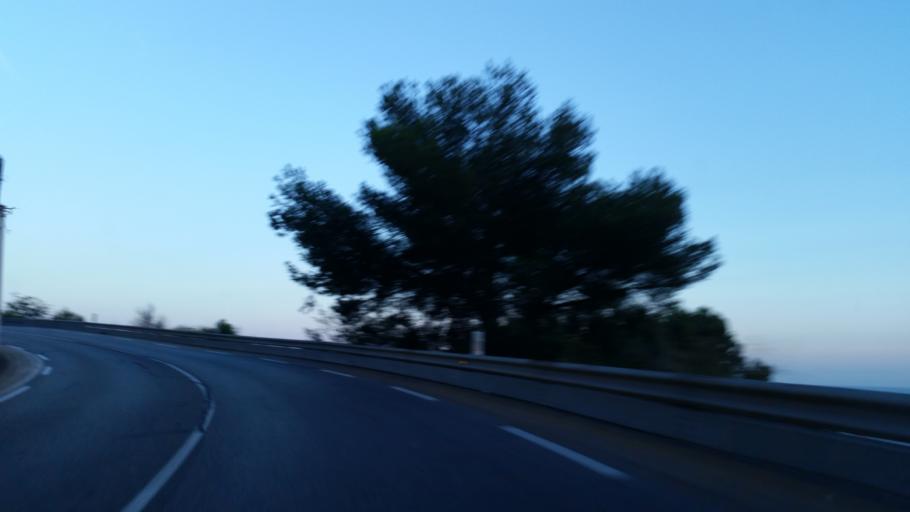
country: MC
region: Commune de Monaco
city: Saint-Roman
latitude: 43.7563
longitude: 7.4379
